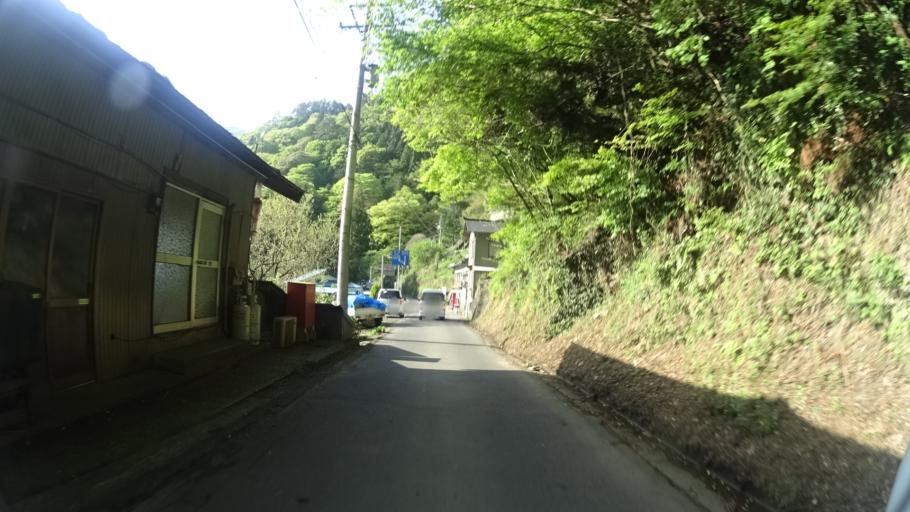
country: JP
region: Tokushima
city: Ikedacho
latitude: 33.8807
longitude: 133.9321
